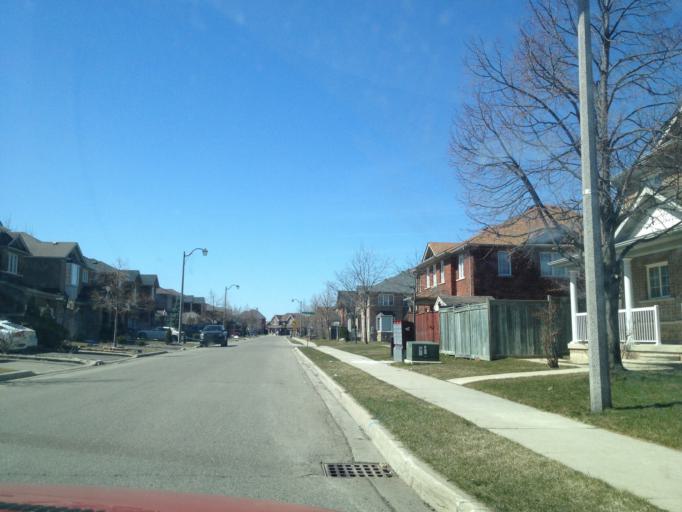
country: CA
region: Ontario
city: Brampton
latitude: 43.6870
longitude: -79.8129
